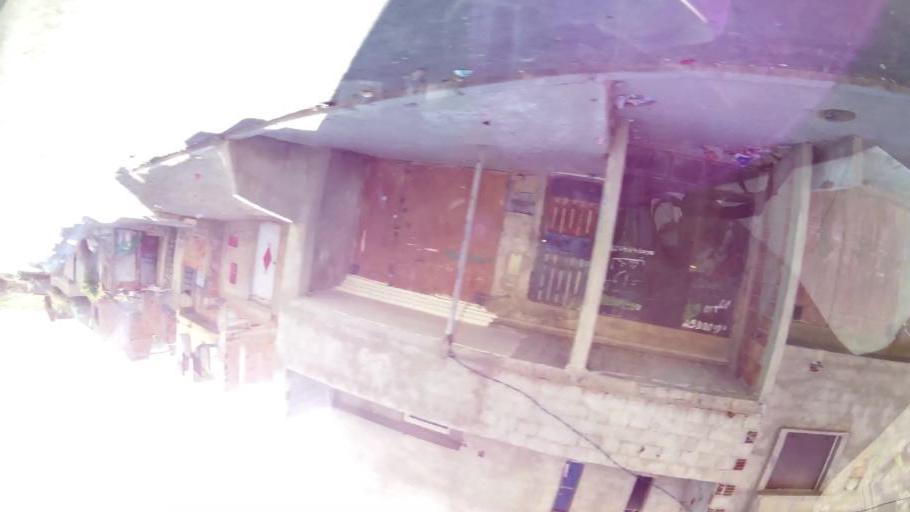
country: MA
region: Oriental
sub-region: Oujda-Angad
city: Oujda
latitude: 34.6451
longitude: -1.9485
